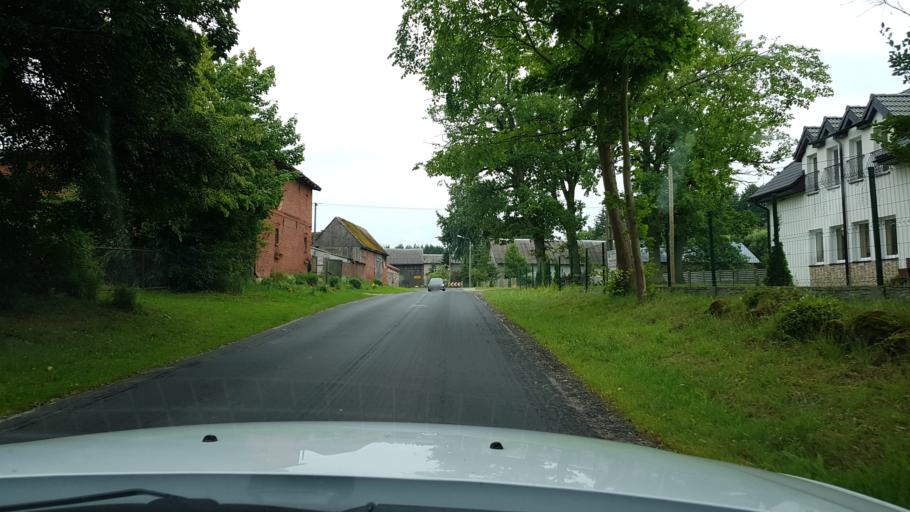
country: PL
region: West Pomeranian Voivodeship
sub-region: Powiat slawienski
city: Slawno
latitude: 54.4890
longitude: 16.5818
